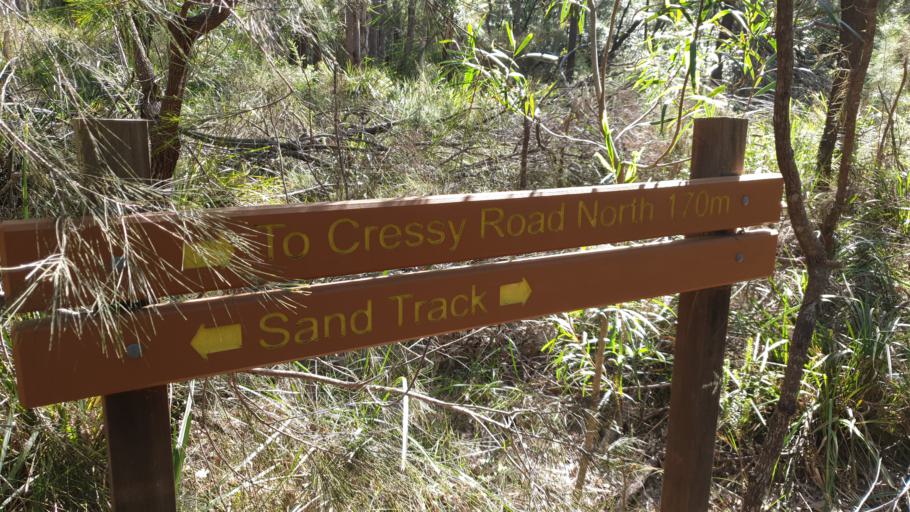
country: AU
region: New South Wales
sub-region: Ryde
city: East Ryde
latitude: -33.8108
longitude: 151.1281
